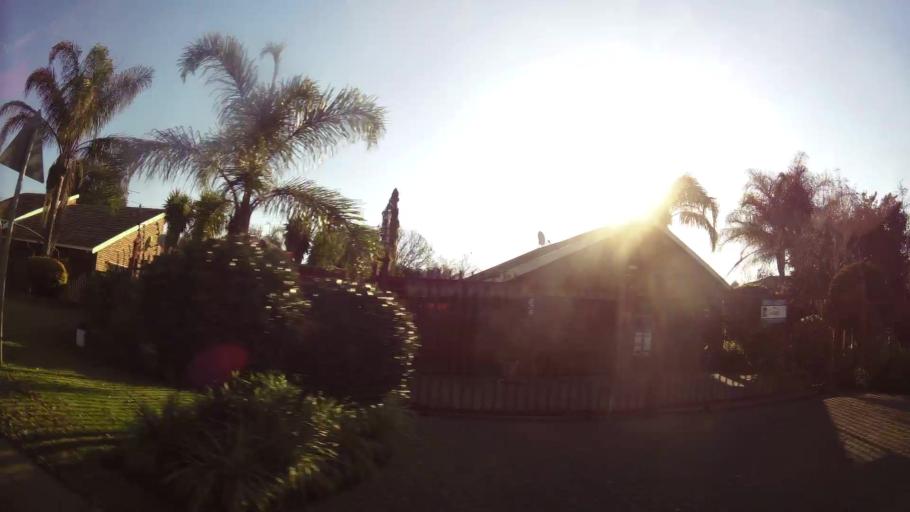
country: ZA
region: Gauteng
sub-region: City of Tshwane Metropolitan Municipality
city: Centurion
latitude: -25.8656
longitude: 28.1524
